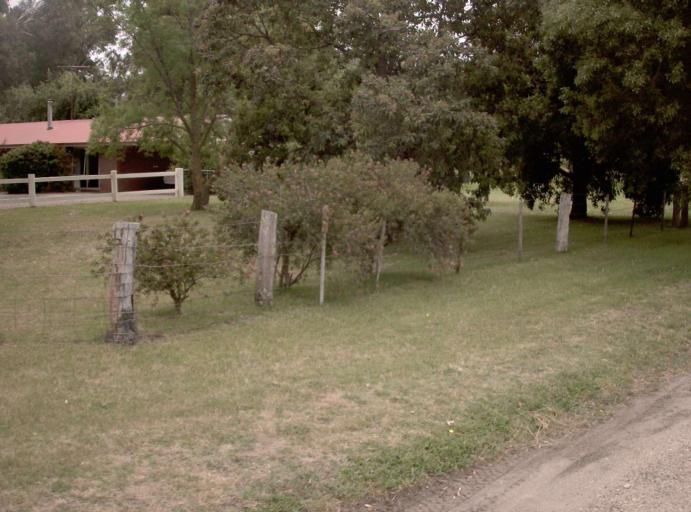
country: AU
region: Victoria
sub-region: East Gippsland
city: Bairnsdale
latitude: -37.8319
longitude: 147.4332
